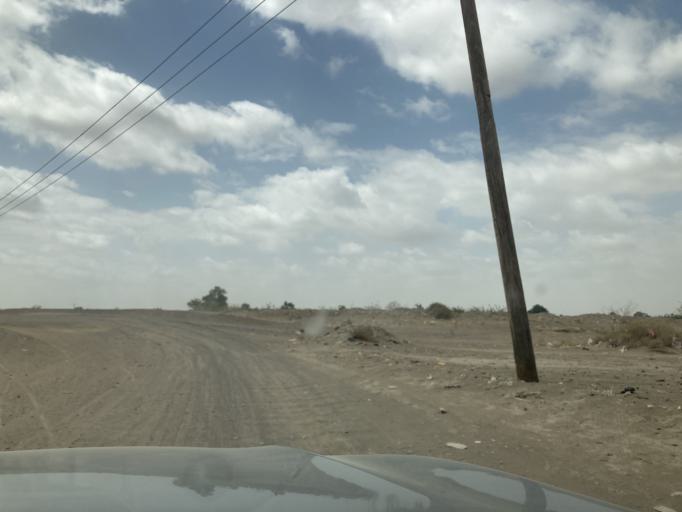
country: YE
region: Lahij
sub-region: Al  Hawtah
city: Lahij
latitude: 13.0209
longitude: 45.0020
